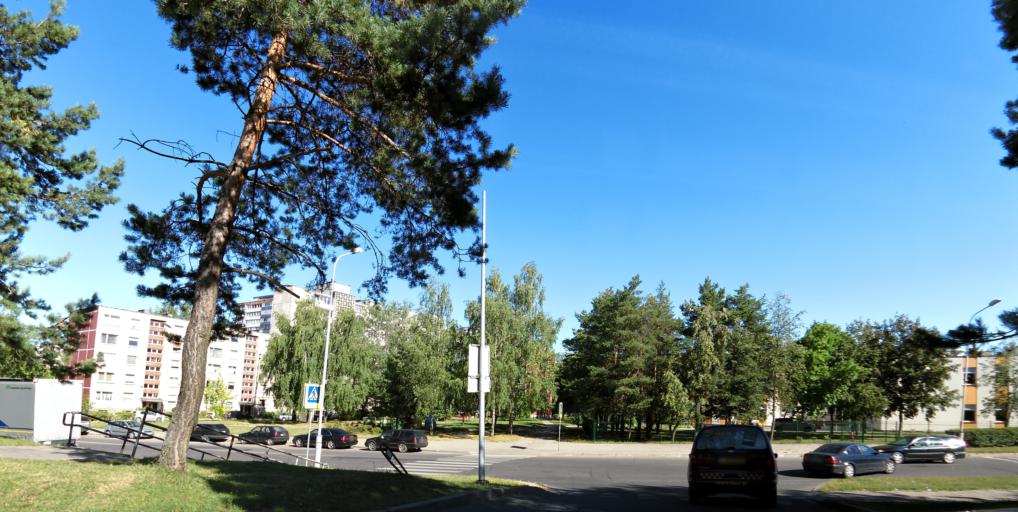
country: LT
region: Vilnius County
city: Justiniskes
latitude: 54.6939
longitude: 25.2225
